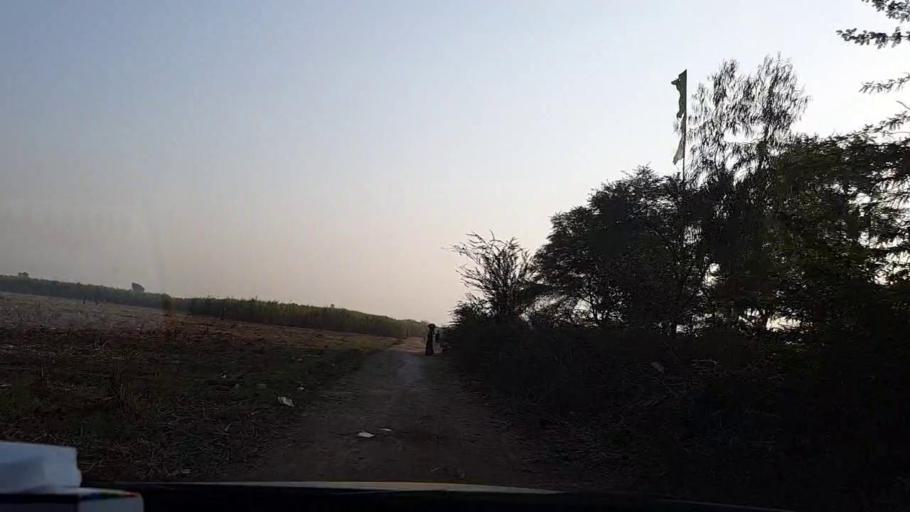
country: PK
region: Sindh
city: Tando Ghulam Ali
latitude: 25.2027
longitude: 68.9208
